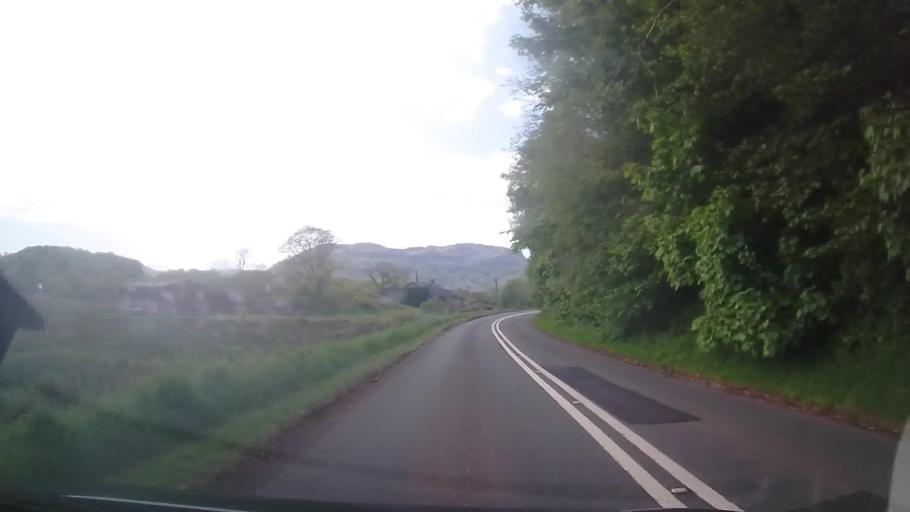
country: GB
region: Wales
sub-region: Gwynedd
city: Porthmadog
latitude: 52.9422
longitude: -4.1339
